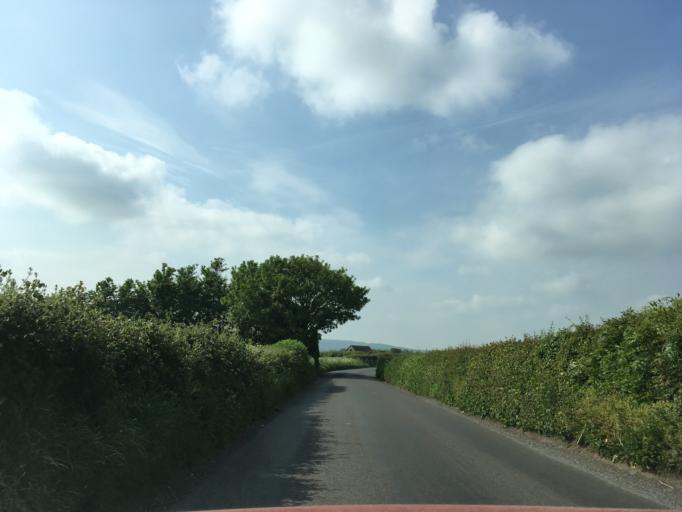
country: GB
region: England
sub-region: North Somerset
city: Brockley
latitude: 51.4197
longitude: -2.7776
